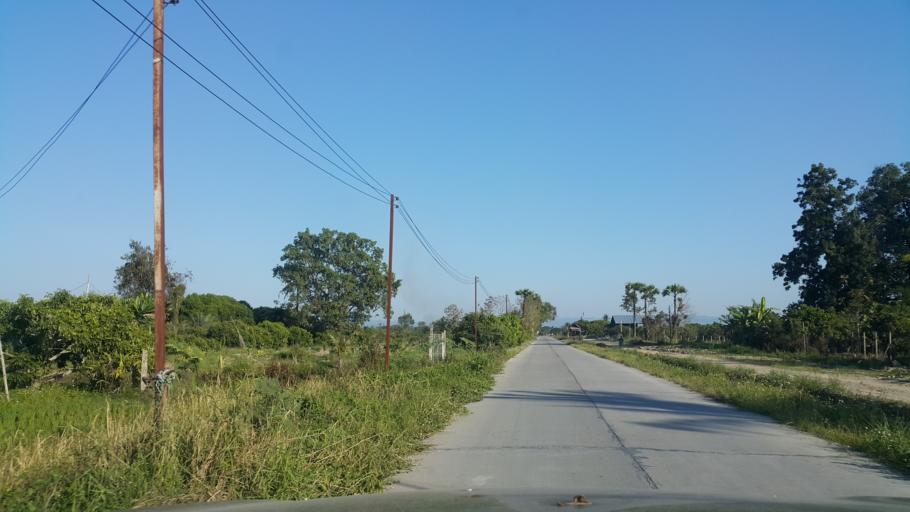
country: TH
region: Chiang Mai
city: Hang Dong
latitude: 18.6777
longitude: 98.9586
